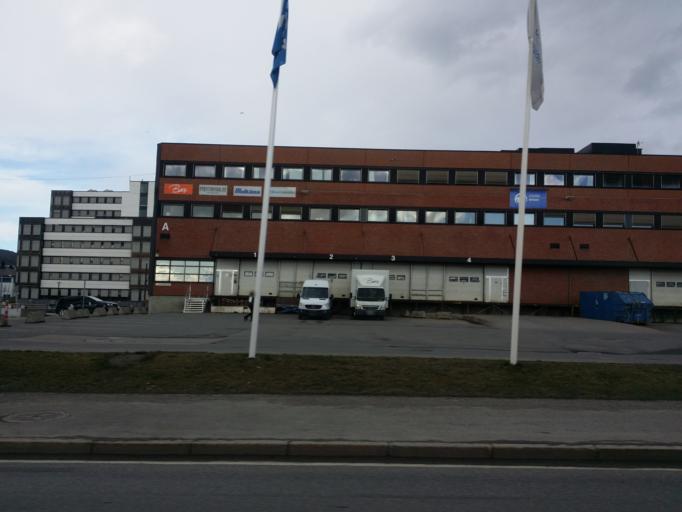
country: NO
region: Oslo
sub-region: Oslo
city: Oslo
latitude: 59.9257
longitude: 10.8115
